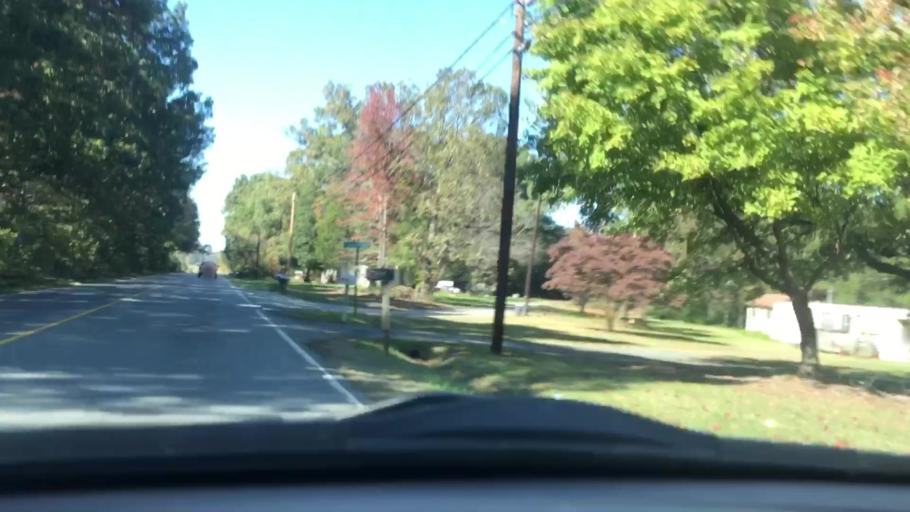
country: US
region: North Carolina
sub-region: Randolph County
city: Randleman
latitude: 35.8165
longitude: -79.8436
